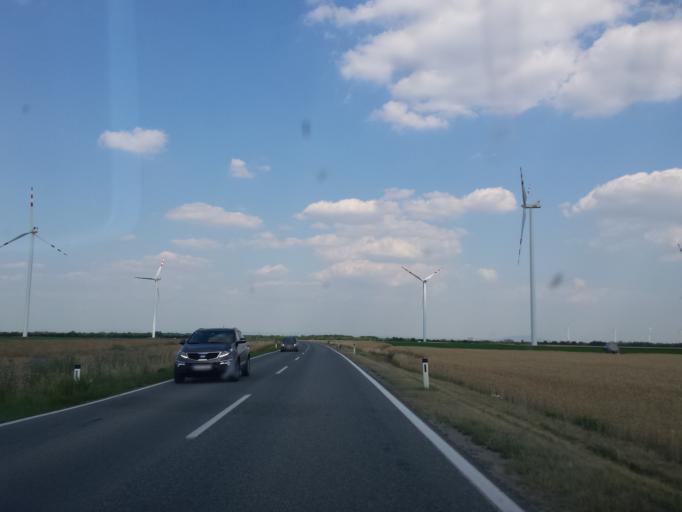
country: AT
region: Lower Austria
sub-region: Politischer Bezirk Ganserndorf
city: Glinzendorf
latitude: 48.2622
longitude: 16.6589
